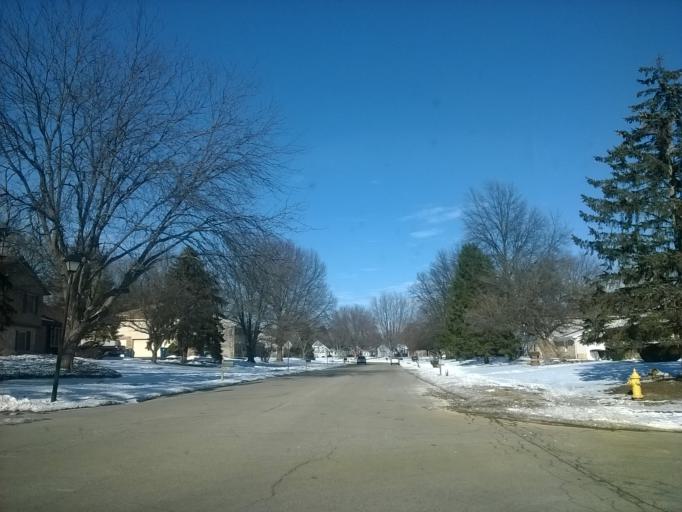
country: US
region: Indiana
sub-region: Hamilton County
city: Carmel
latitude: 39.9436
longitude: -86.1042
